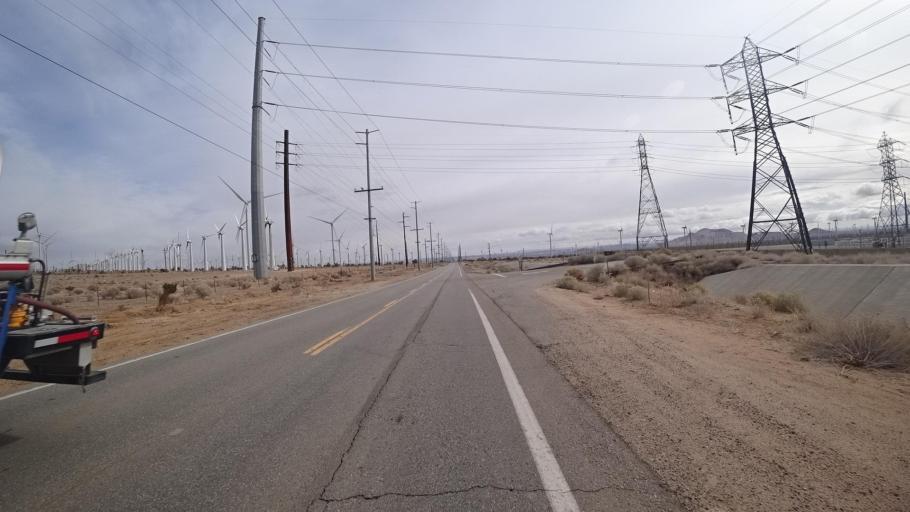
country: US
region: California
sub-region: Kern County
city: Mojave
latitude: 35.0383
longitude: -118.2808
